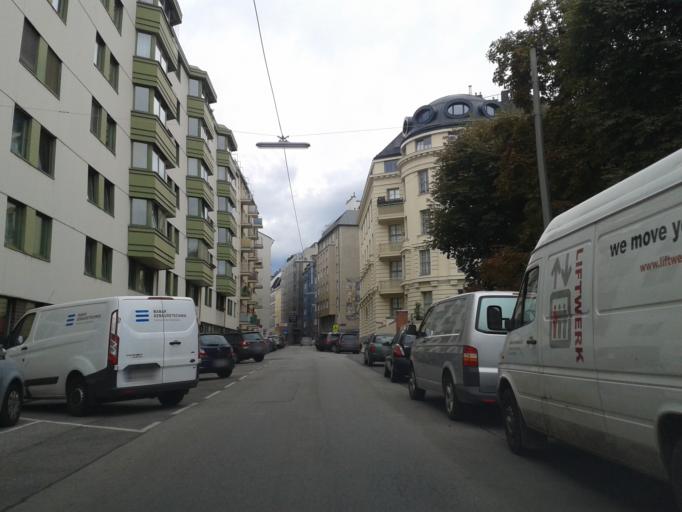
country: AT
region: Vienna
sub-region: Wien Stadt
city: Vienna
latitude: 48.1950
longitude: 16.3943
